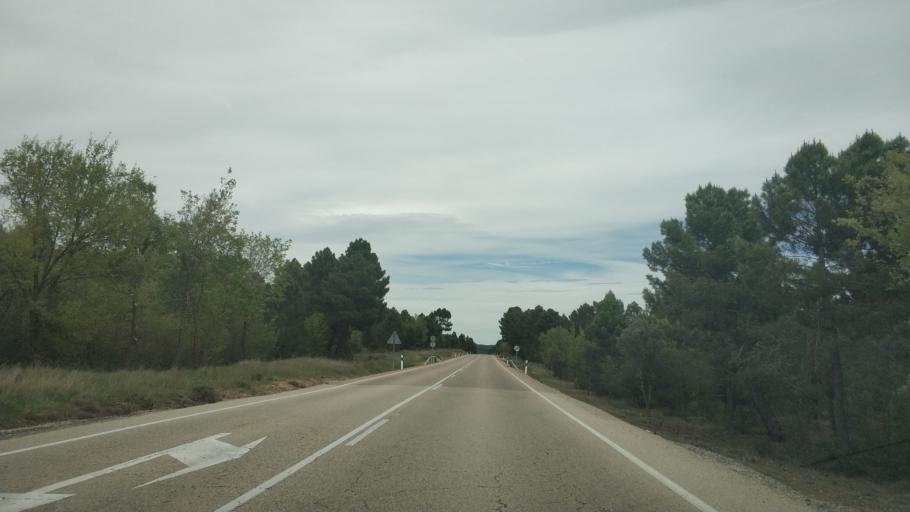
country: ES
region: Castille and Leon
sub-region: Provincia de Soria
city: Bayubas de Abajo
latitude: 41.5107
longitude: -2.9205
